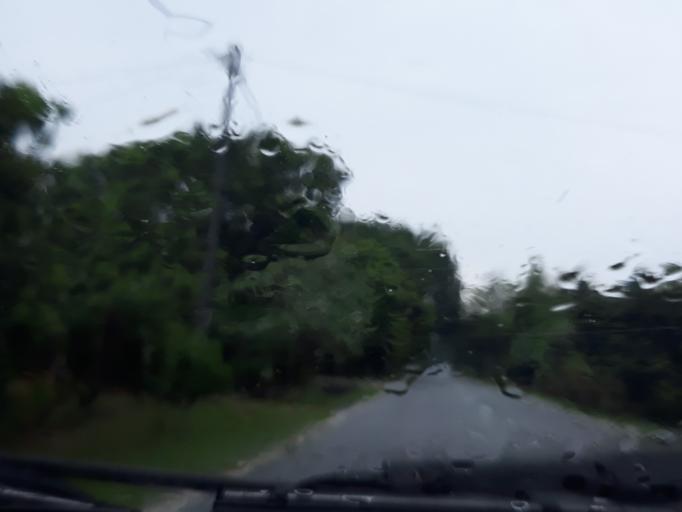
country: MY
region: Penang
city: Nibong Tebal
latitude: 5.2277
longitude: 100.6064
